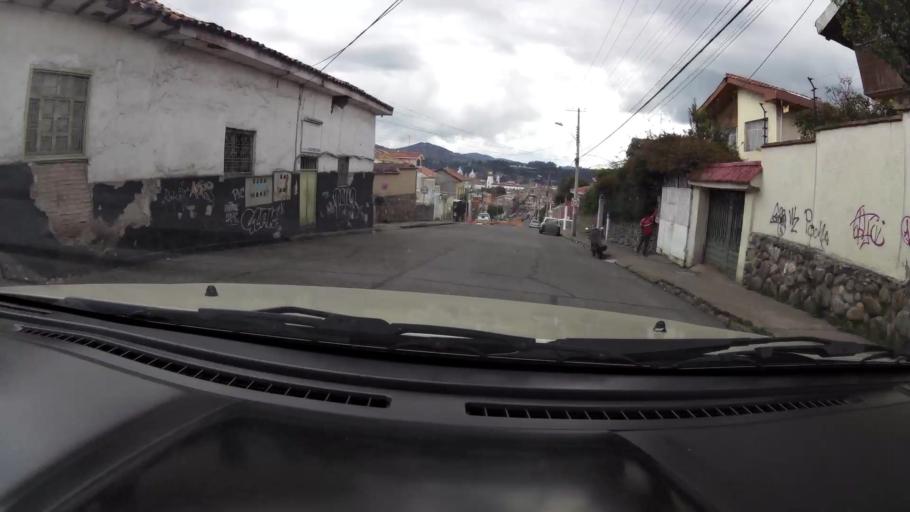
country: EC
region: Azuay
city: Cuenca
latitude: -2.8883
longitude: -79.0054
